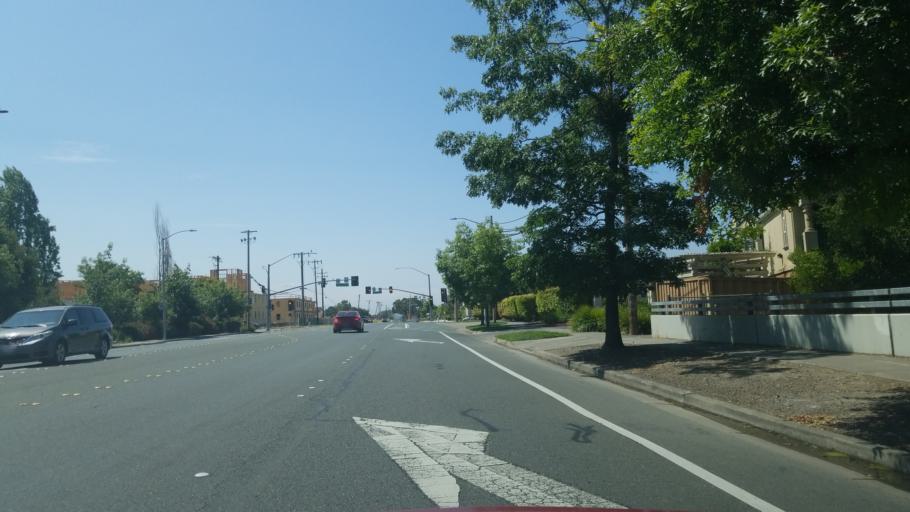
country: US
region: California
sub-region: Sonoma County
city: Roseland
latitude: 38.4175
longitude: -122.7043
